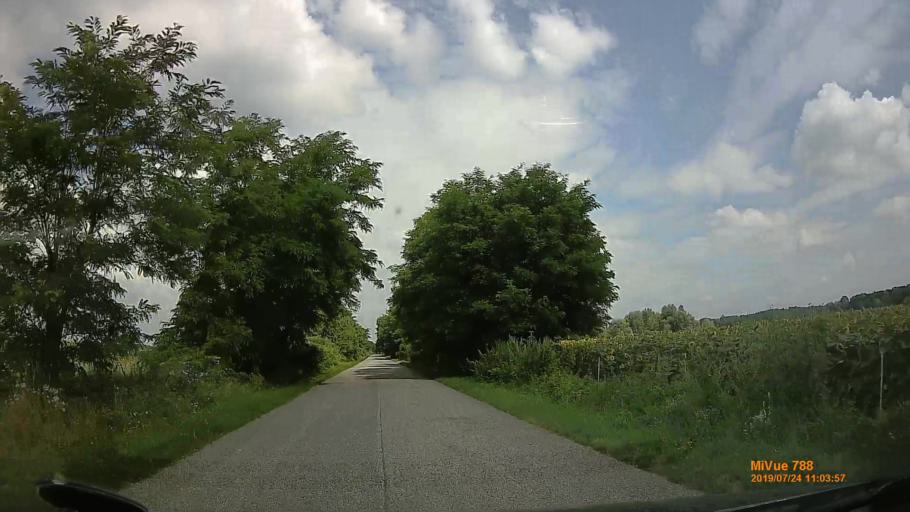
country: HU
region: Szabolcs-Szatmar-Bereg
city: Tarpa
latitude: 48.1645
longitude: 22.5161
